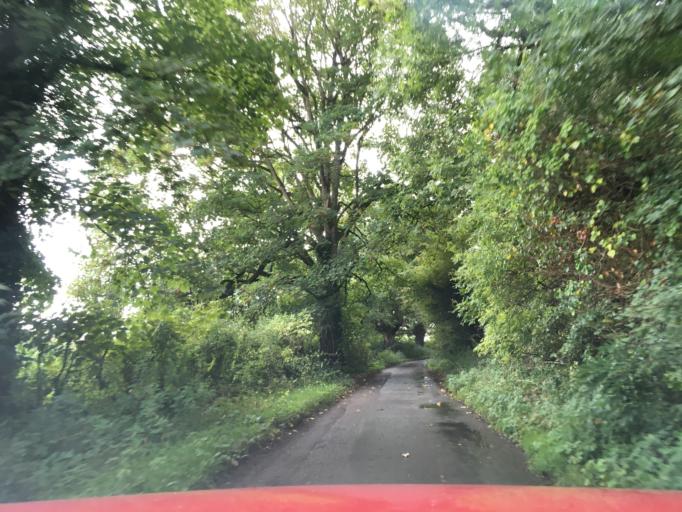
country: GB
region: England
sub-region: South Gloucestershire
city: Tytherington
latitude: 51.5966
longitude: -2.4704
